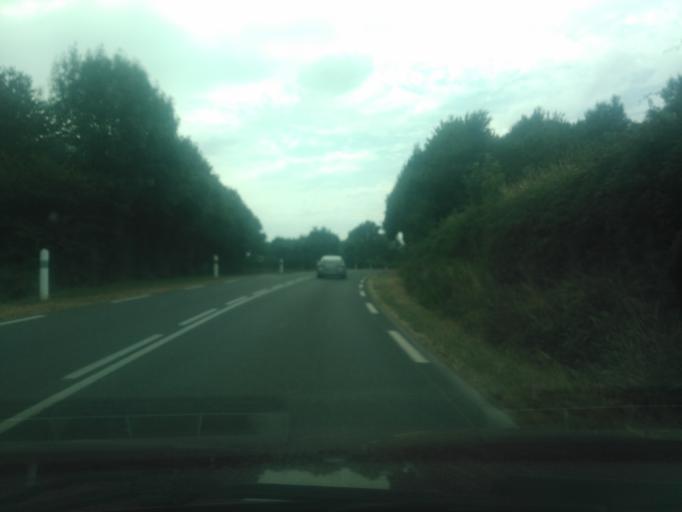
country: FR
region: Pays de la Loire
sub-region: Departement de la Vendee
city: Saint-Pierre-du-Chemin
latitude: 46.6468
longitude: -0.6437
